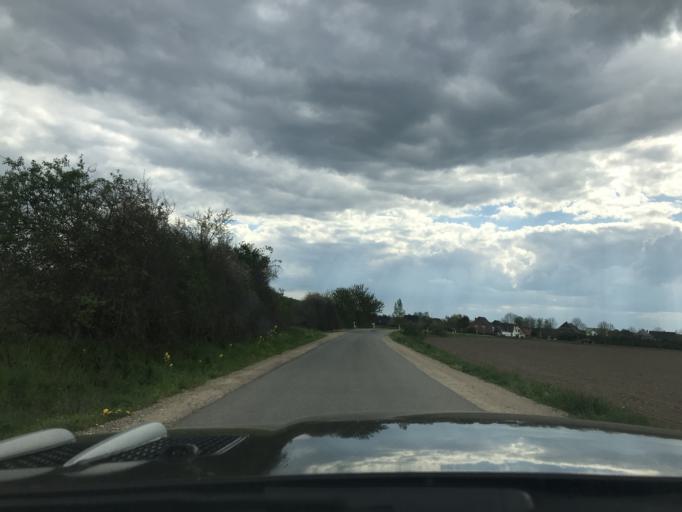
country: DE
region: Schleswig-Holstein
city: Gross Gronau
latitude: 53.7722
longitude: 10.7768
